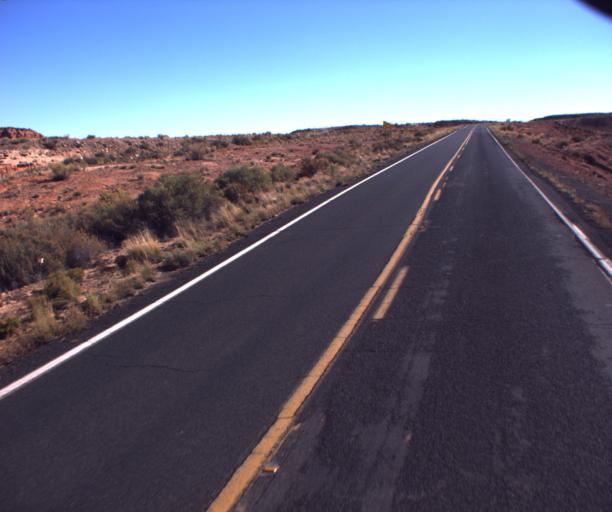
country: US
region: Arizona
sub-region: Coconino County
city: Tuba City
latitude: 36.1025
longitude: -111.2003
